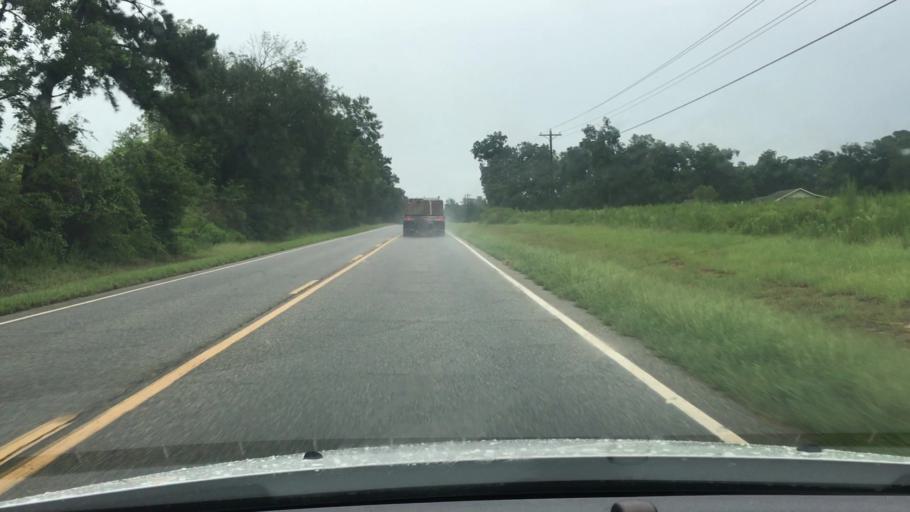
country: US
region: Georgia
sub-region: Grady County
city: Cairo
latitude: 30.8247
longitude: -84.2465
